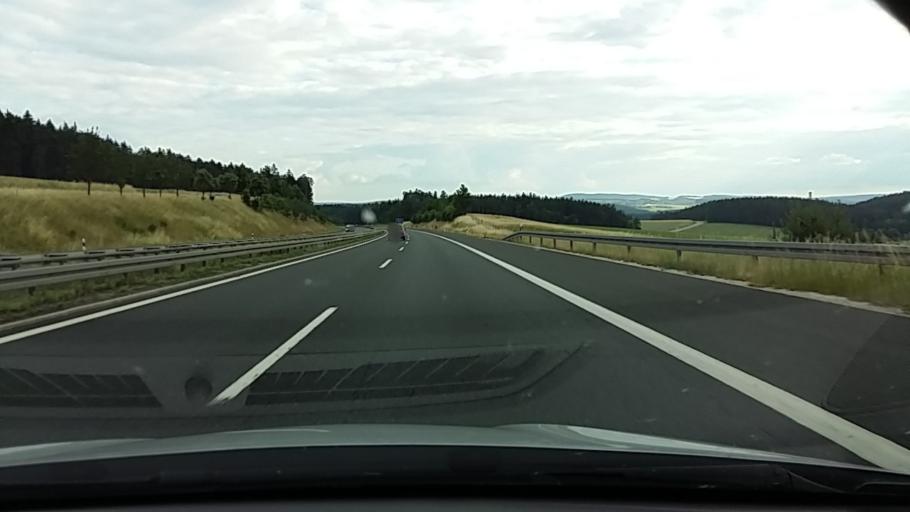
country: DE
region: Bavaria
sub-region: Upper Palatinate
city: Wernberg-Koblitz
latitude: 49.5551
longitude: 12.1974
